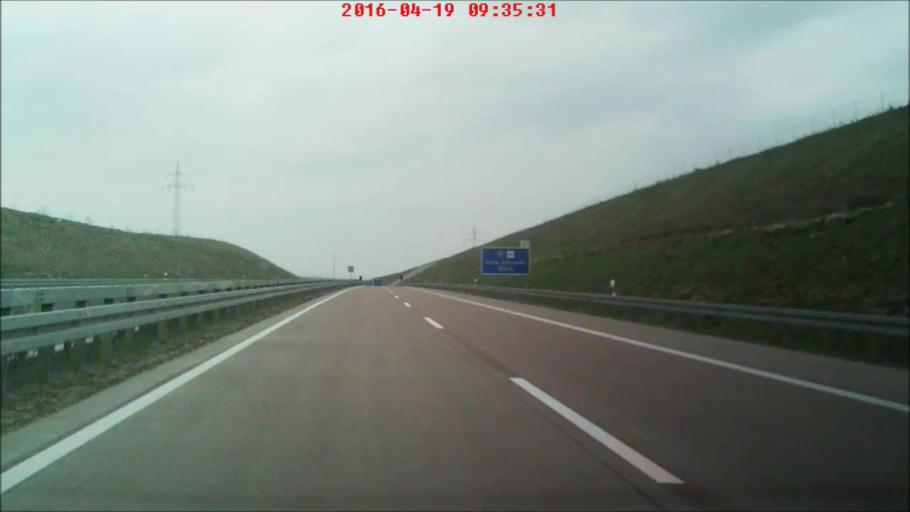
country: DE
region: Thuringia
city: Bretleben
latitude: 51.3232
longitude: 11.2432
